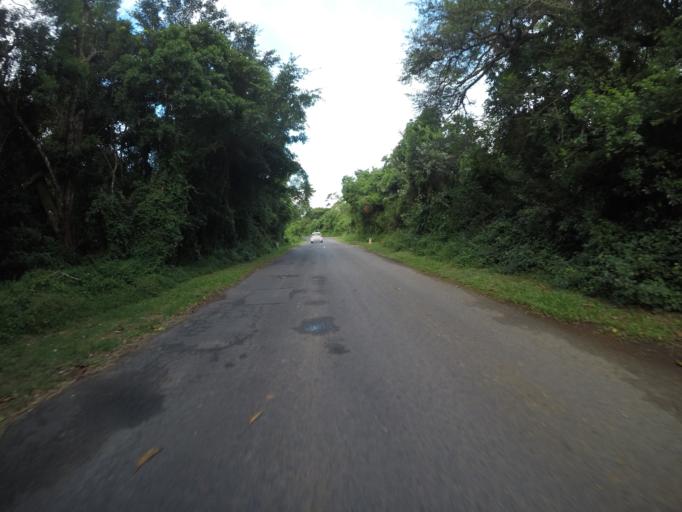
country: ZA
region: KwaZulu-Natal
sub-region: uMkhanyakude District Municipality
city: Mtubatuba
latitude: -28.3849
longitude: 32.4142
